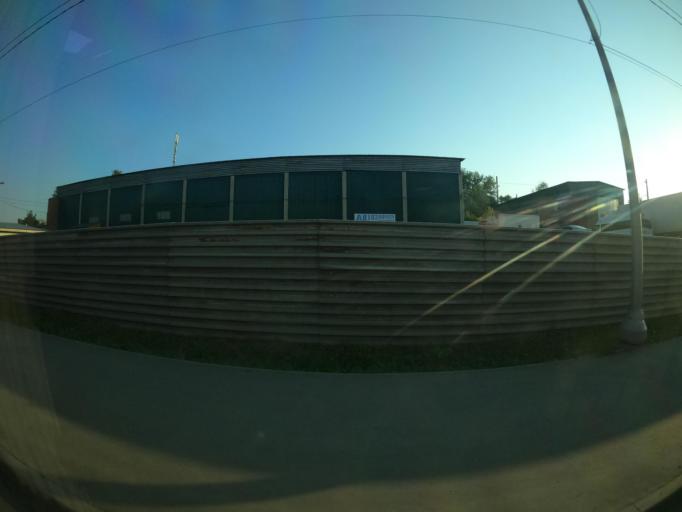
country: RU
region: Moskovskaya
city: Serpukhov
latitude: 54.9220
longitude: 37.3811
